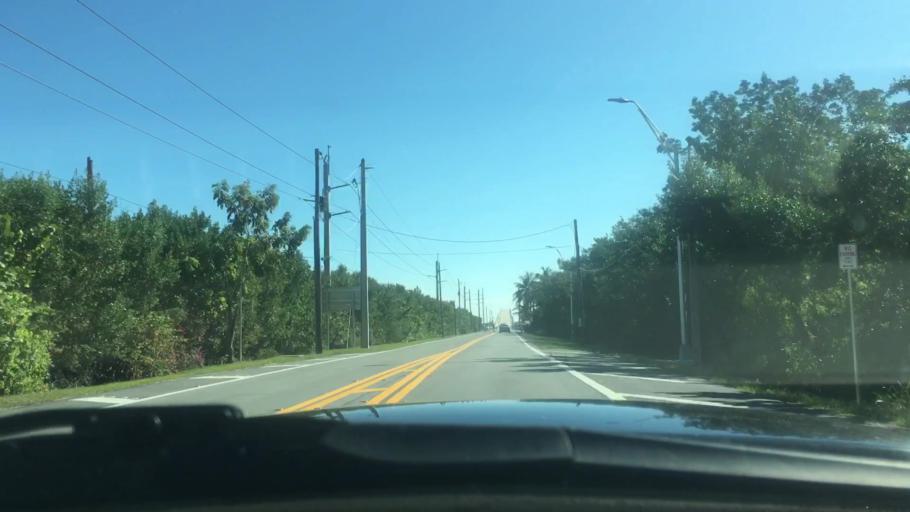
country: US
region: Florida
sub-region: Monroe County
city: North Key Largo
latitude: 25.2909
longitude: -80.3772
